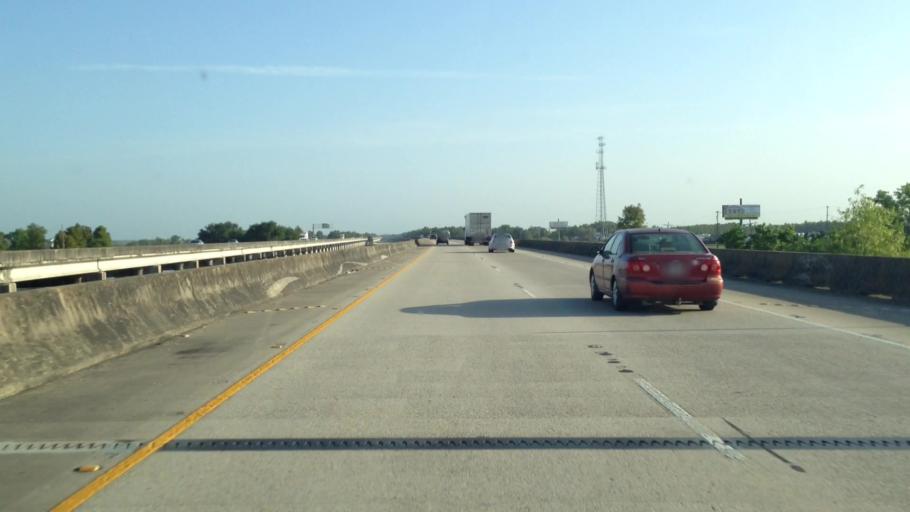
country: US
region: Louisiana
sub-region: Tangipahoa Parish
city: Ponchatoula
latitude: 30.3099
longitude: -90.4066
